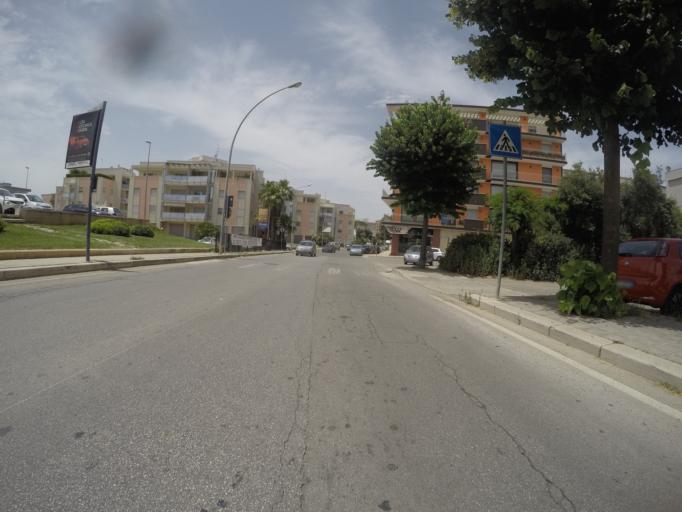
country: IT
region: Apulia
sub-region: Provincia di Taranto
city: Martina Franca
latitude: 40.6971
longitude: 17.3398
